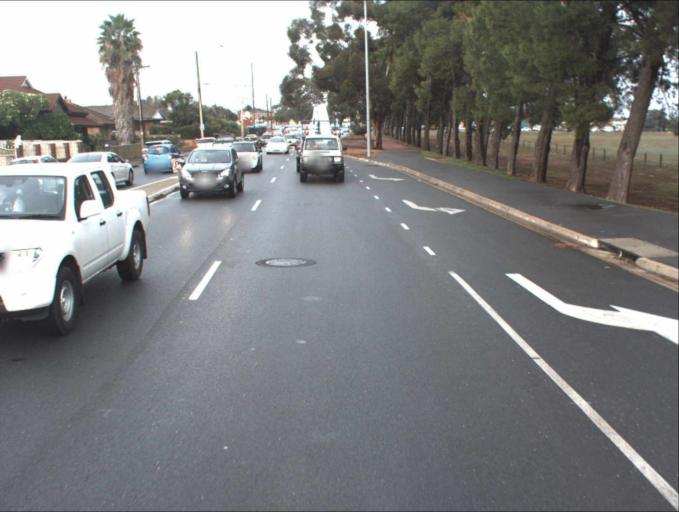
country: AU
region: South Australia
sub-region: Port Adelaide Enfield
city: Enfield
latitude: -34.8454
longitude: 138.6186
